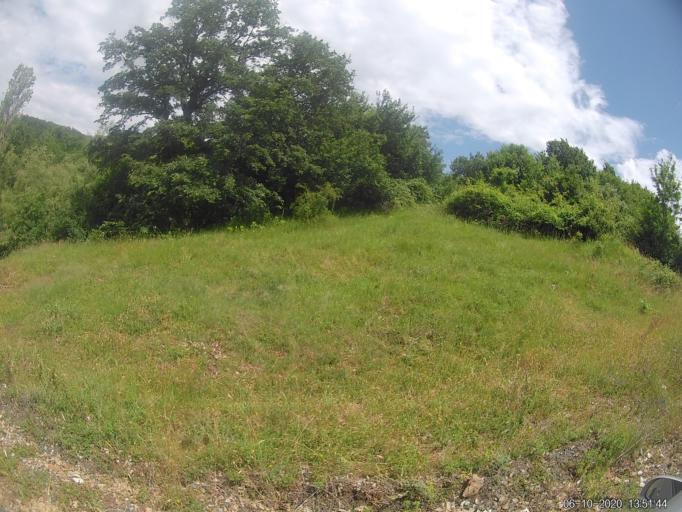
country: XK
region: Prizren
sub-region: Komuna e Therandes
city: Budakovo
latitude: 42.4047
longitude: 20.9258
